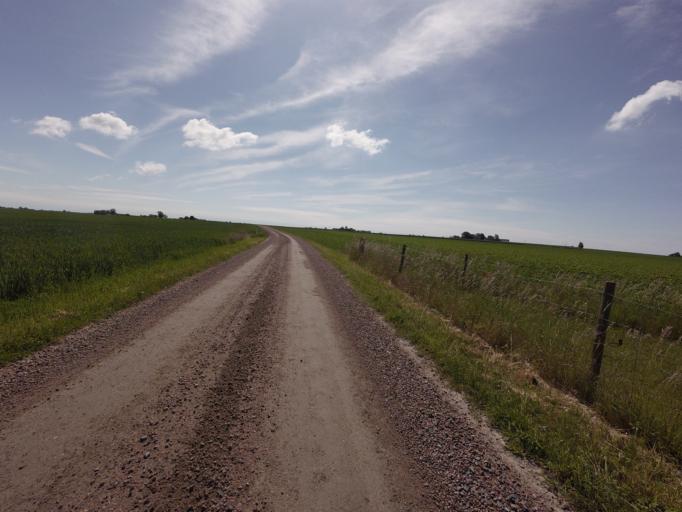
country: SE
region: Skane
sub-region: Trelleborgs Kommun
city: Skare
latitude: 55.4153
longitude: 13.0352
